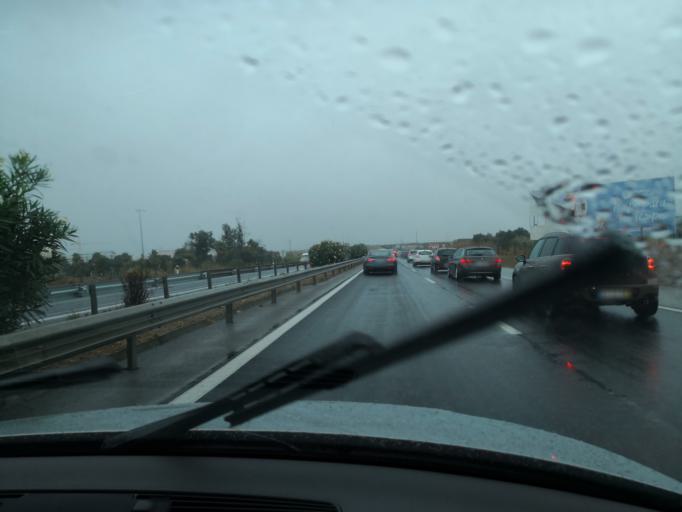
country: PT
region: Setubal
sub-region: Montijo
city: Montijo
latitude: 38.6955
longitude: -8.9394
